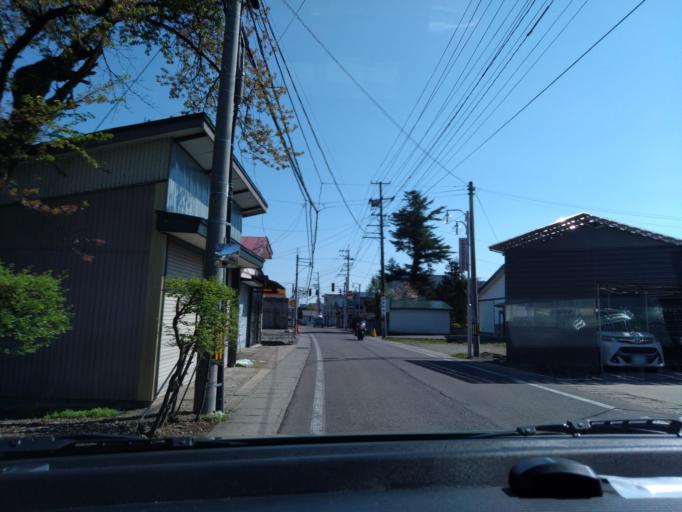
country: JP
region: Akita
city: Kakunodatemachi
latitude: 39.5019
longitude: 140.5945
